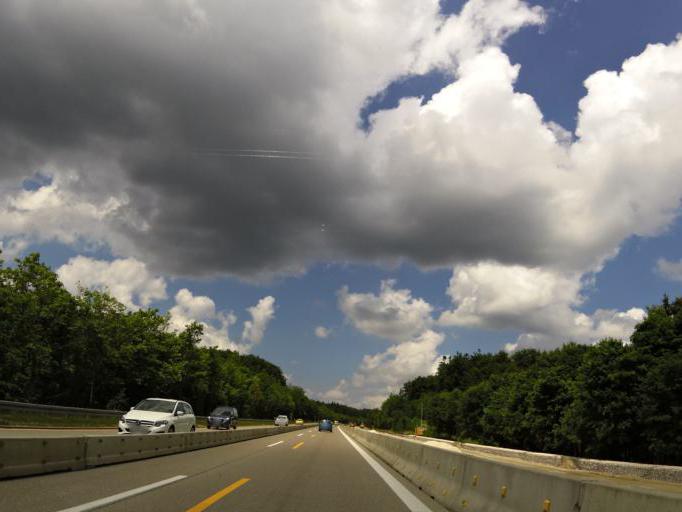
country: DE
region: Baden-Wuerttemberg
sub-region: Regierungsbezirk Stuttgart
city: Nattheim
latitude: 48.6748
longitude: 10.2210
